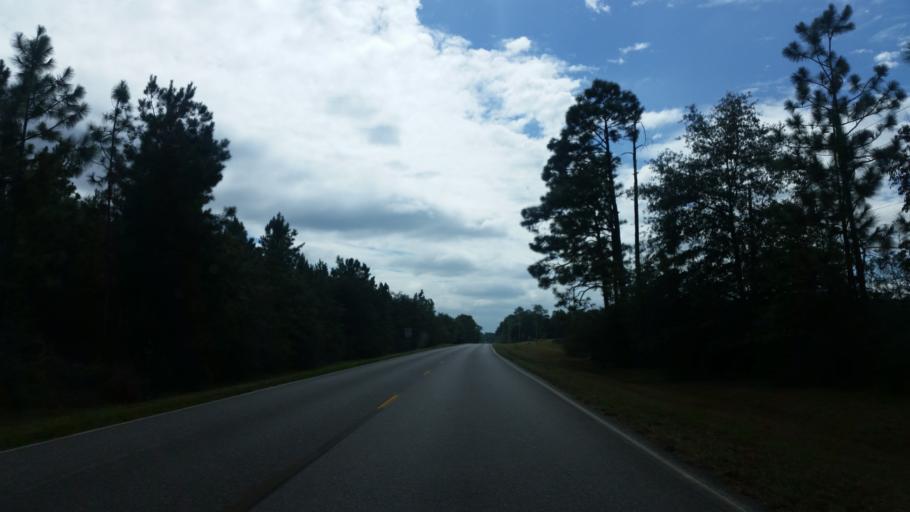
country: US
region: Florida
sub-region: Santa Rosa County
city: Point Baker
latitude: 30.7733
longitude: -86.9409
